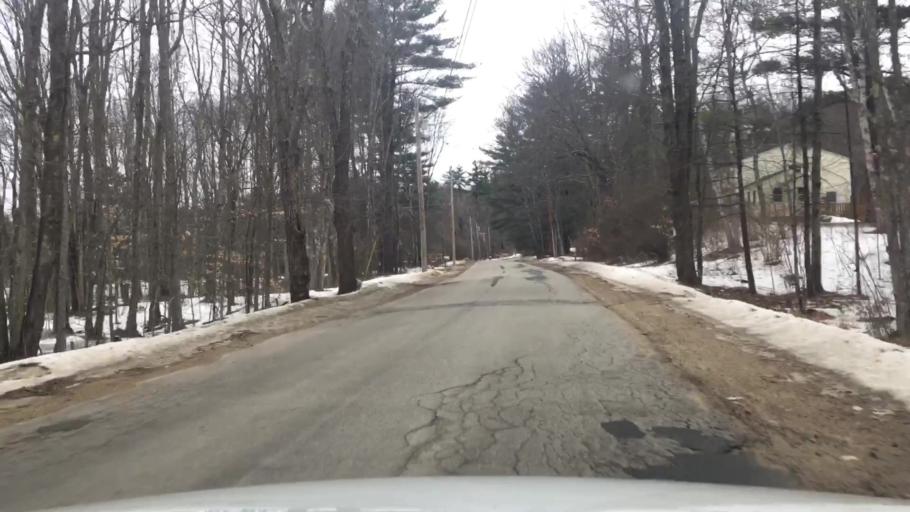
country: US
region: New Hampshire
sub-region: Strafford County
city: Rochester
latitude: 43.3531
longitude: -70.9658
